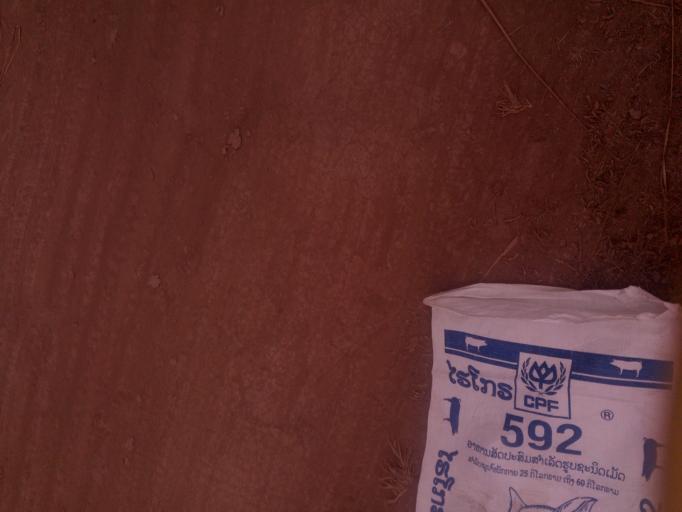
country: LA
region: Xiangkhoang
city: Muang Phonsavan
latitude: 19.3398
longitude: 103.6064
